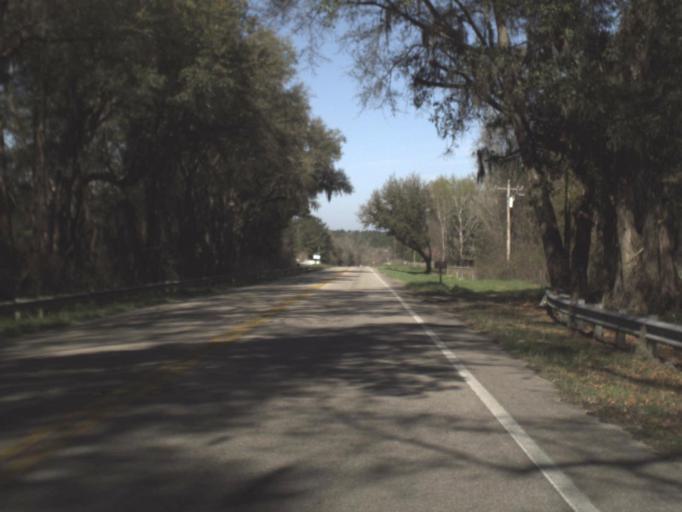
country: US
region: Florida
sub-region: Jefferson County
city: Monticello
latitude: 30.3719
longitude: -83.9948
